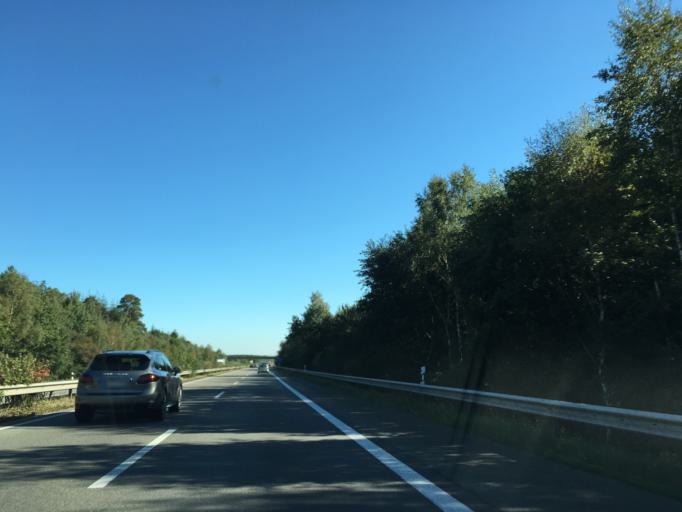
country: DE
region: Lower Saxony
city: Radbruch
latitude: 53.3332
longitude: 10.2590
